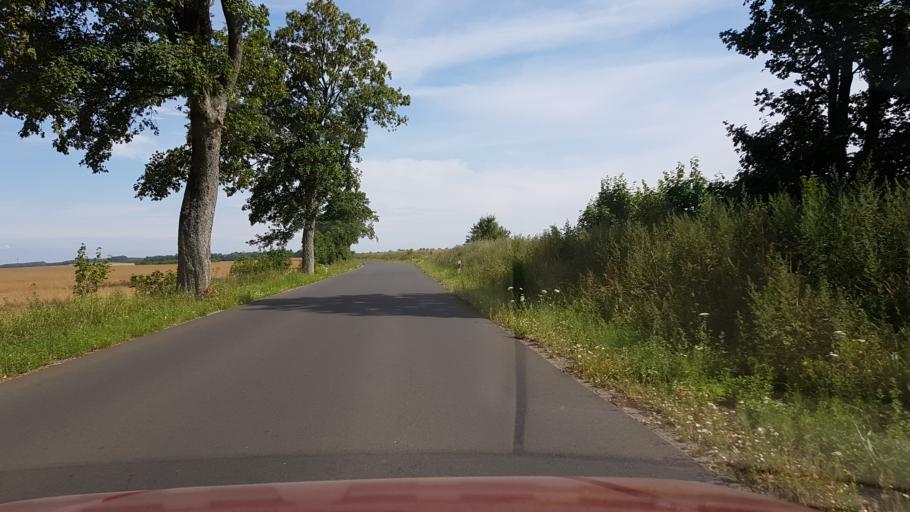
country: PL
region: West Pomeranian Voivodeship
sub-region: Powiat koszalinski
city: Polanow
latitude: 54.1375
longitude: 16.6204
